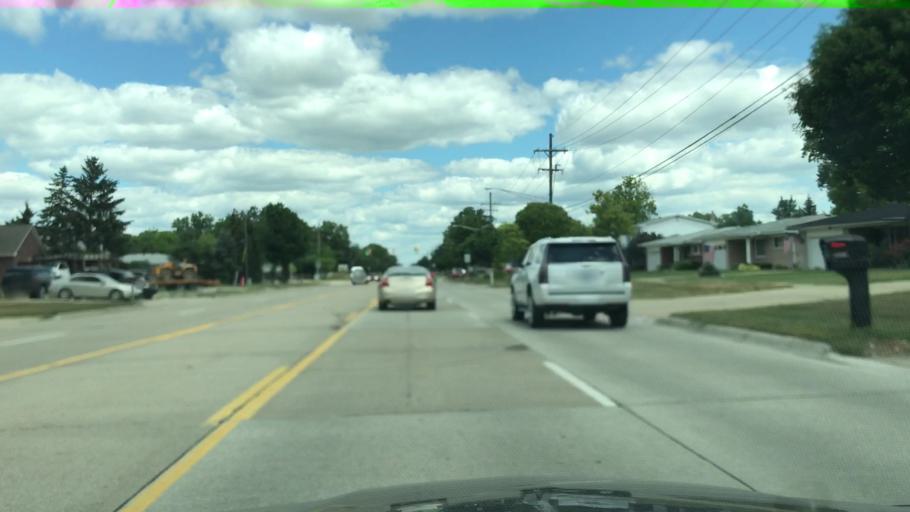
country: US
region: Michigan
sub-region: Macomb County
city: Sterling Heights
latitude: 42.5409
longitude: -83.0688
